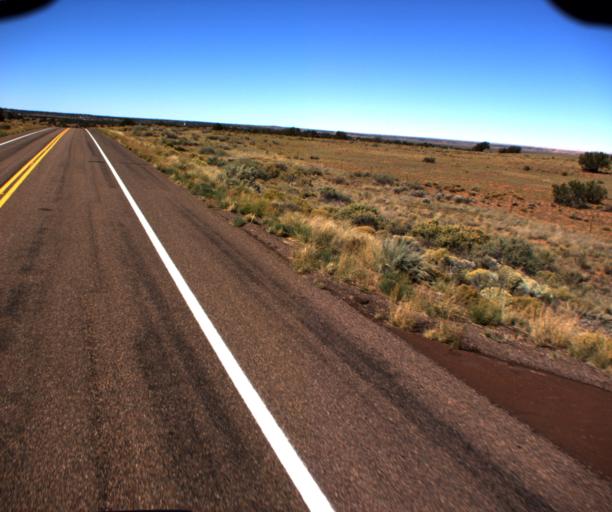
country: US
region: Arizona
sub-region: Apache County
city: Saint Johns
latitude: 34.5950
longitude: -109.6222
